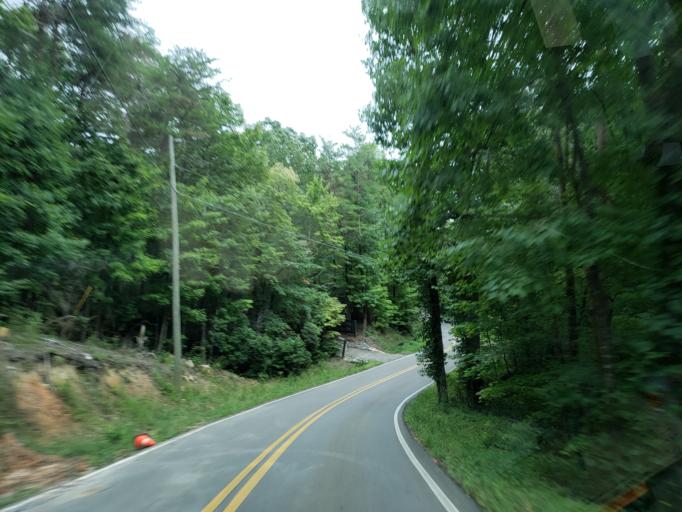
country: US
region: Georgia
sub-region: Pickens County
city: Jasper
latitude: 34.4176
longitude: -84.5366
